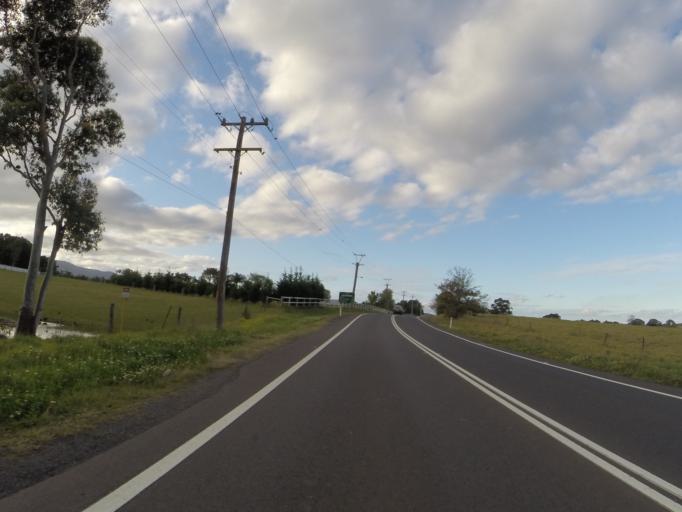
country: AU
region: New South Wales
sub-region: Shellharbour
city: Albion Park Rail
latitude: -34.5678
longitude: 150.7742
